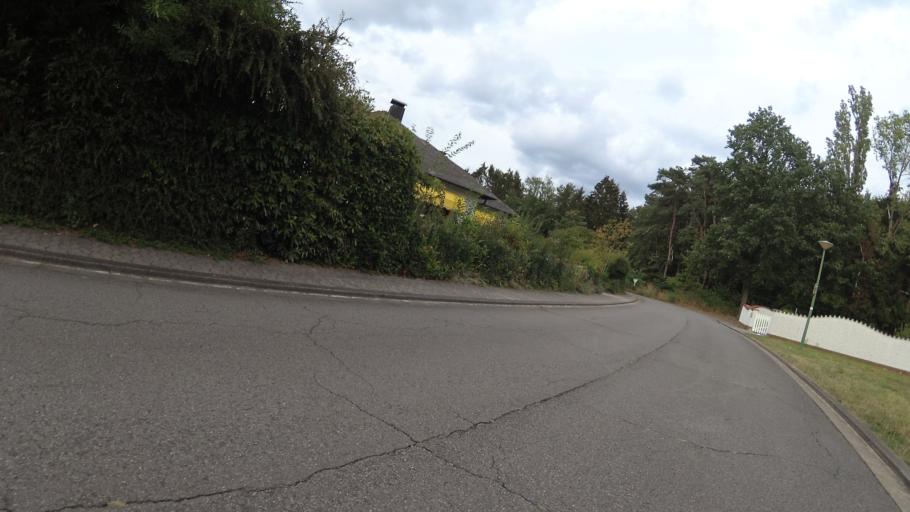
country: DE
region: Saarland
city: Bexbach
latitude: 49.3042
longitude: 7.2774
